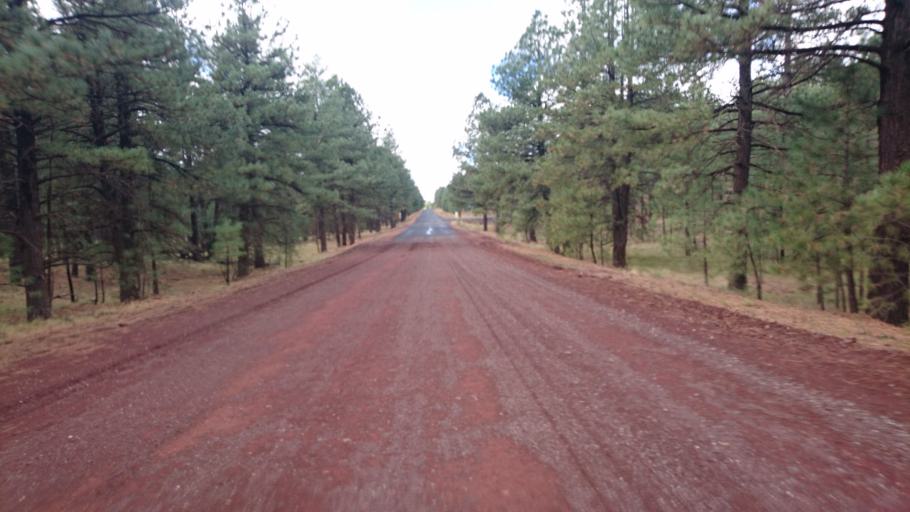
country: US
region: Arizona
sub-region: Coconino County
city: Parks
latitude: 35.2614
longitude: -111.9218
